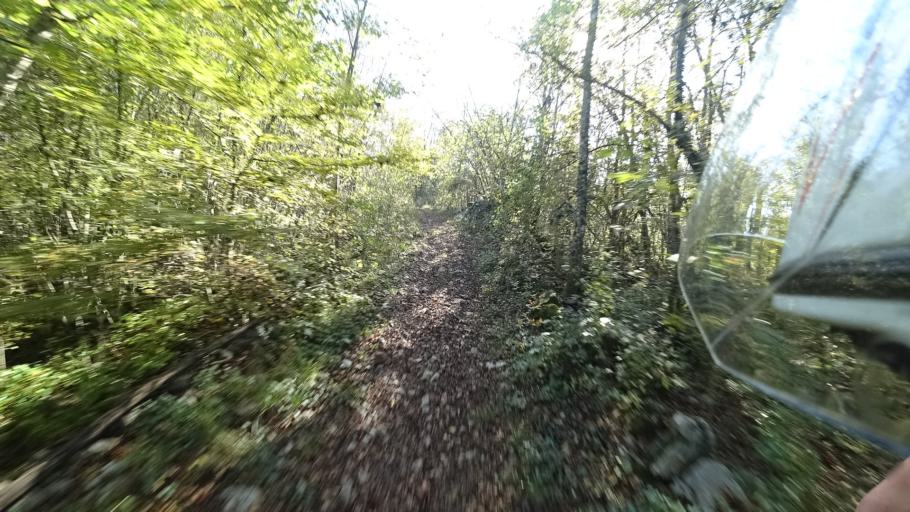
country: HR
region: Primorsko-Goranska
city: Matulji
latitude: 45.3965
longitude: 14.2968
